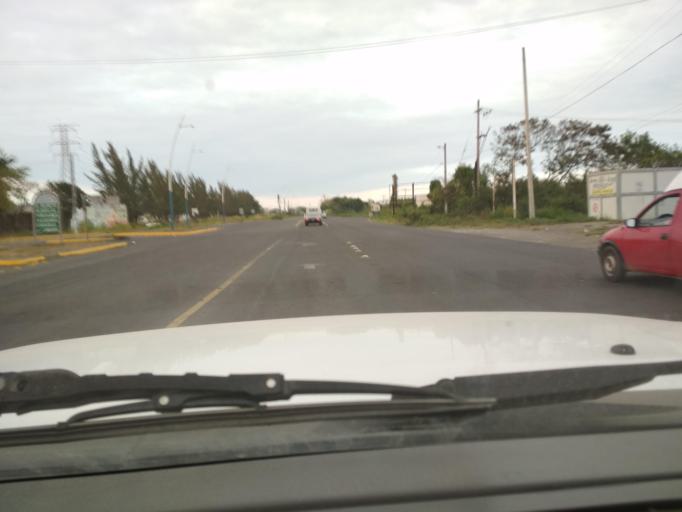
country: MX
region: Veracruz
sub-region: Medellin
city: Fraccionamiento Arboledas San Ramon
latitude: 19.0919
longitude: -96.1528
